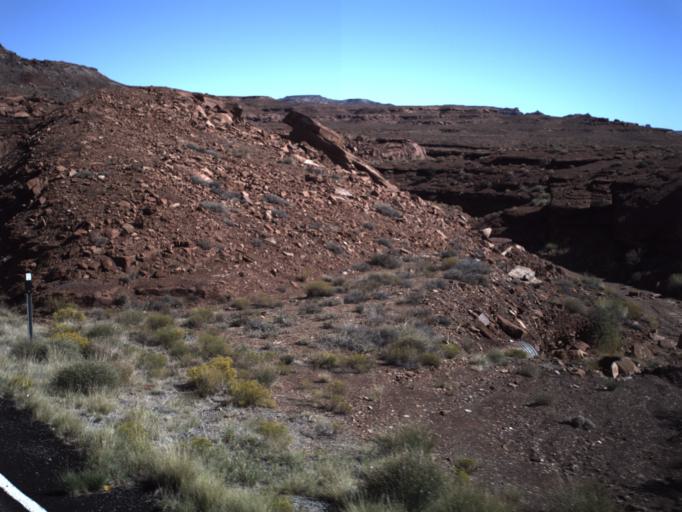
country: US
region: Utah
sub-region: San Juan County
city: Blanding
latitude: 37.8887
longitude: -110.4149
